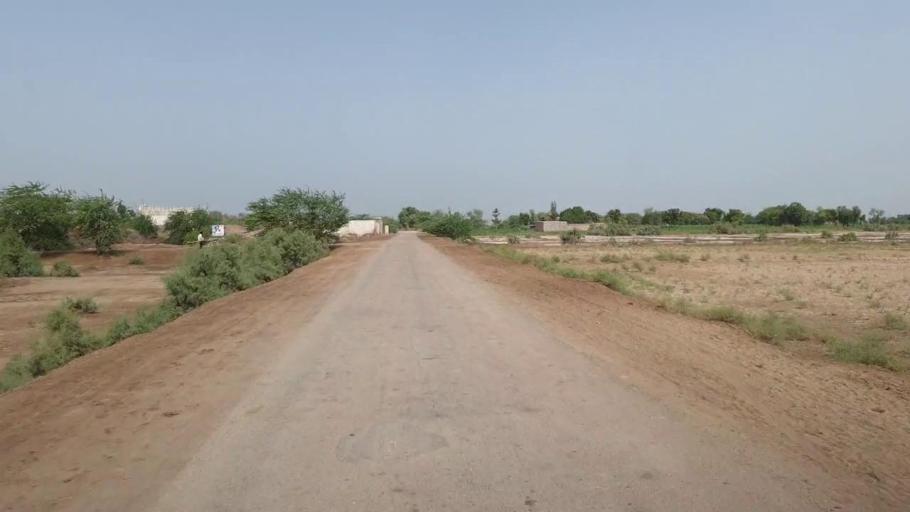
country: PK
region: Sindh
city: Daulatpur
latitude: 26.5471
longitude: 68.0649
